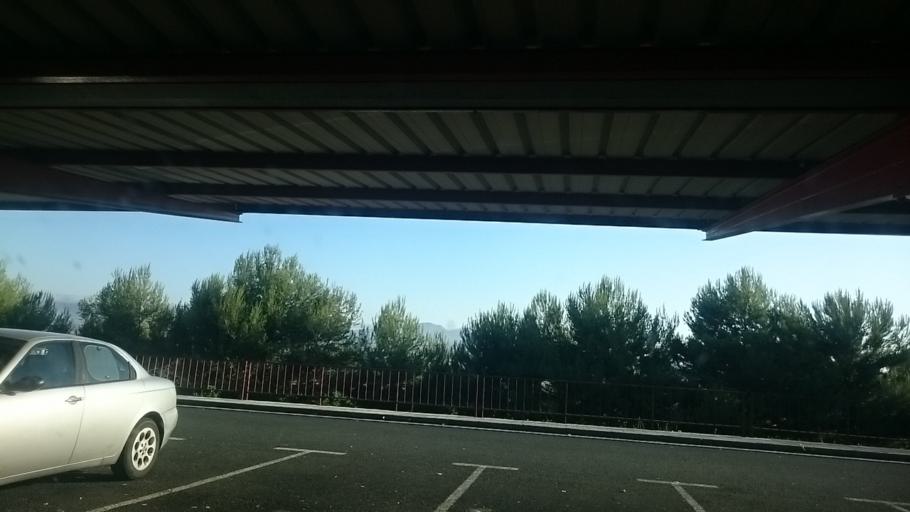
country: ES
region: La Rioja
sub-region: Provincia de La Rioja
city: Villamediana de Iregua
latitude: 42.4503
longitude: -2.3692
